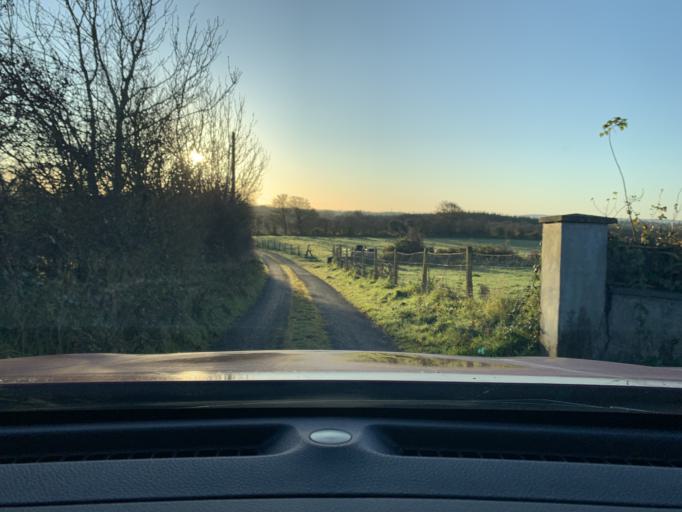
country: IE
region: Connaught
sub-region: Sligo
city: Ballymote
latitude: 54.0632
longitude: -8.5305
